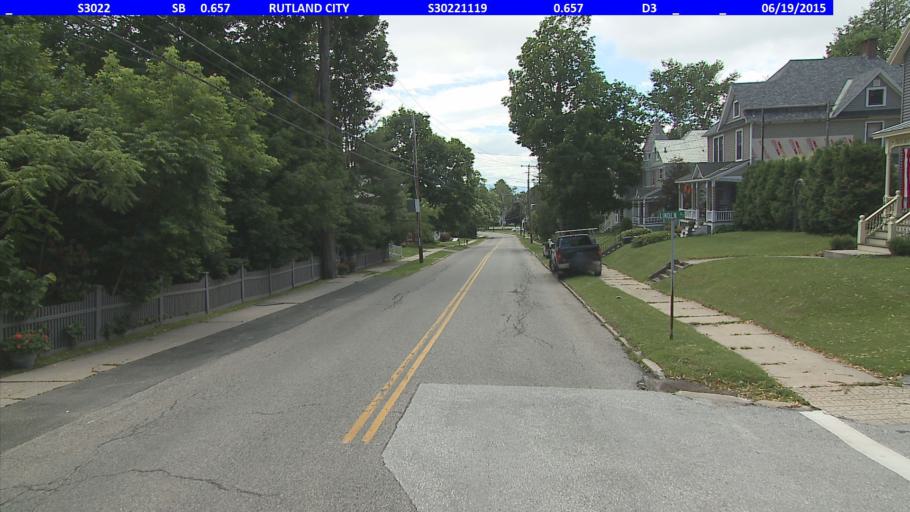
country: US
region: Vermont
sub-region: Rutland County
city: Rutland
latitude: 43.6182
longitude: -72.9846
